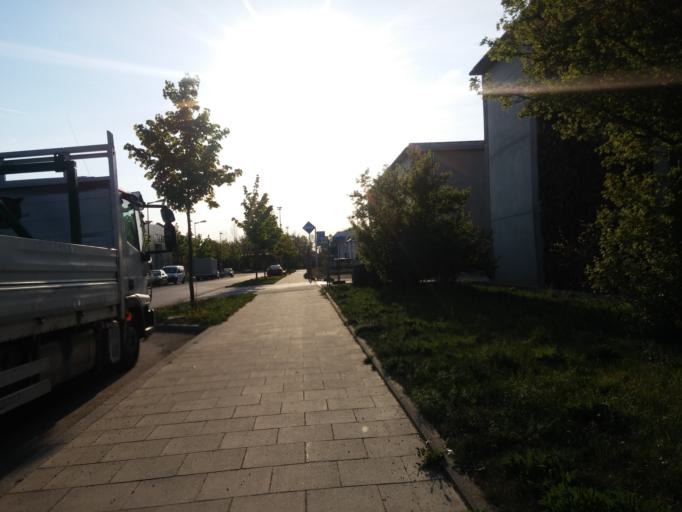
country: DE
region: Bavaria
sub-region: Upper Bavaria
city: Feldkirchen
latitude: 48.1377
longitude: 11.7135
